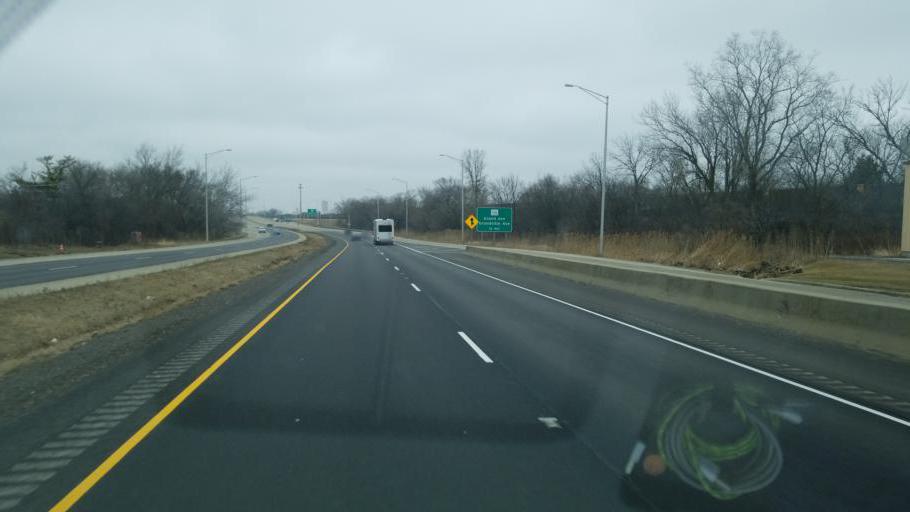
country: US
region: Illinois
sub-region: Lake County
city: Gurnee
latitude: 42.3645
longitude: -87.8947
